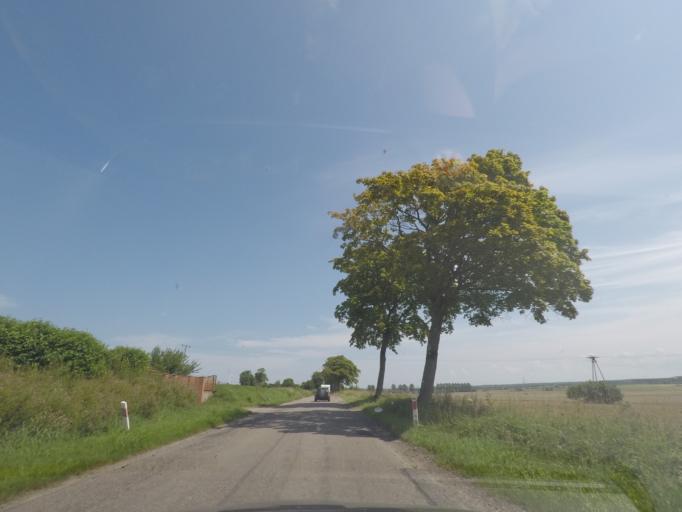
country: PL
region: West Pomeranian Voivodeship
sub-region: Powiat slawienski
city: Darlowo
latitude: 54.4555
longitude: 16.4912
